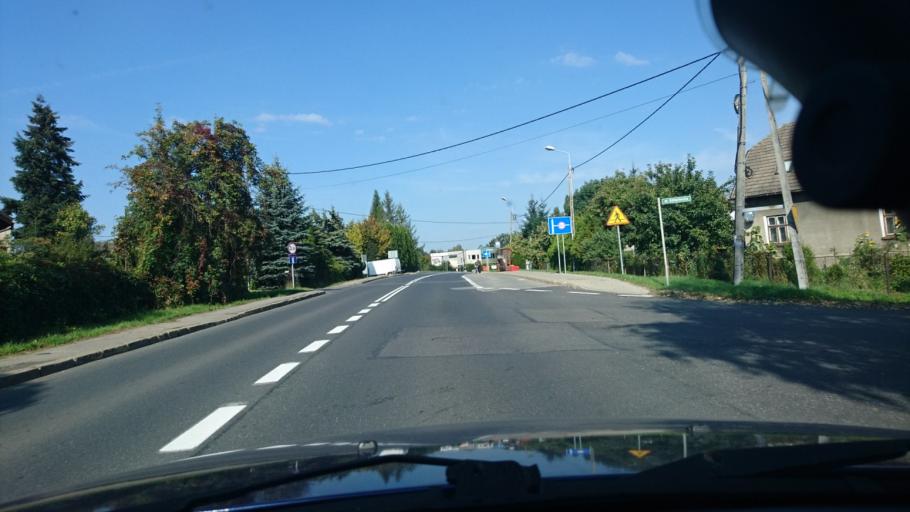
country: PL
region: Silesian Voivodeship
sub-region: Bielsko-Biala
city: Bielsko-Biala
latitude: 49.8599
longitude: 19.0332
